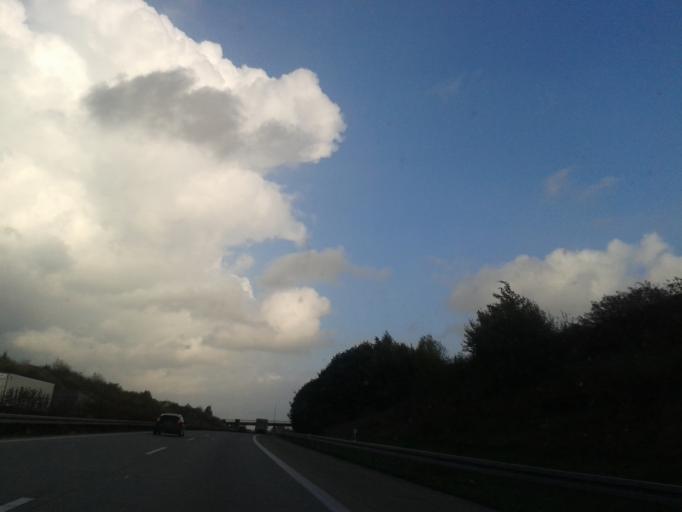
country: DE
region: Saxony
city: Freital
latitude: 51.0367
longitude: 13.6283
